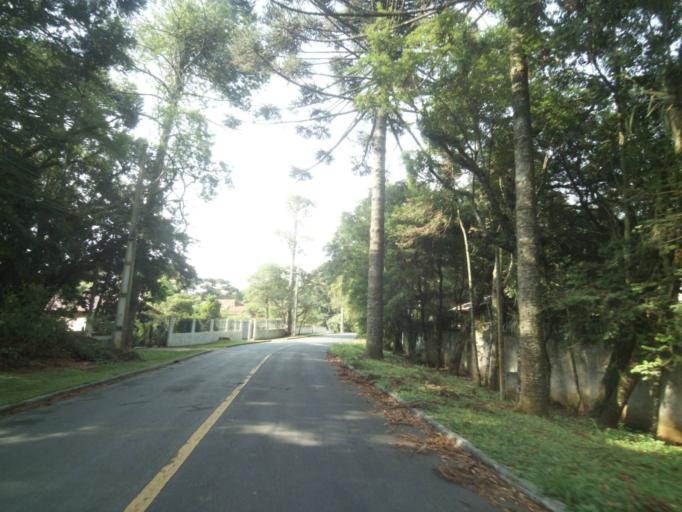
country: BR
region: Parana
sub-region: Curitiba
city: Curitiba
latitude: -25.4109
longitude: -49.3176
